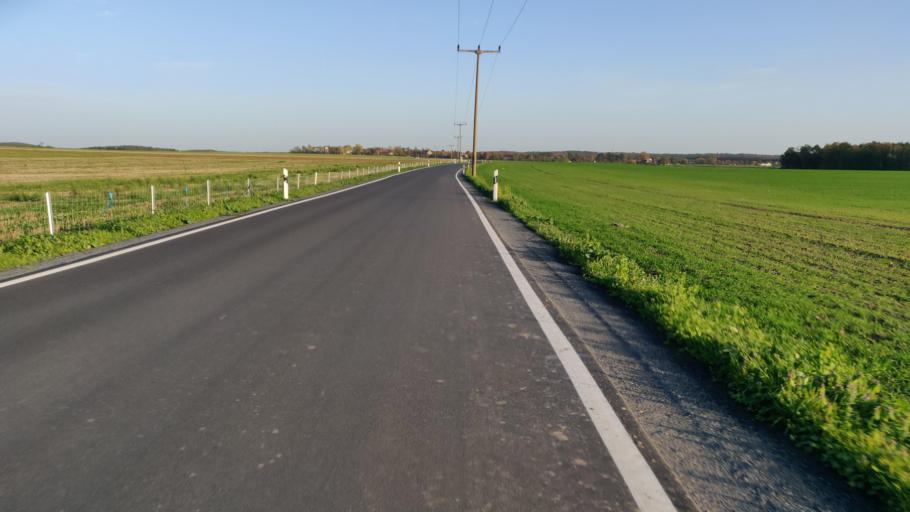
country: DE
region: Brandenburg
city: Hirschfeld
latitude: 51.3519
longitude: 13.6375
